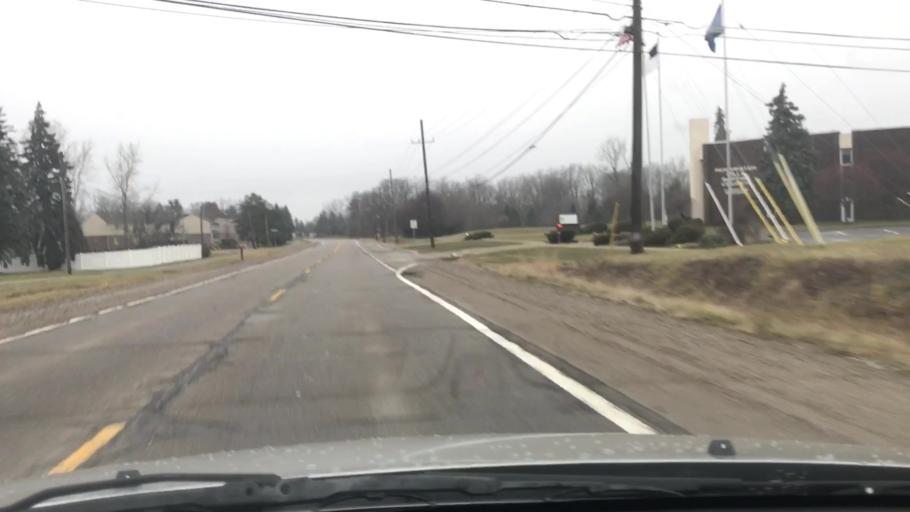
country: US
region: Michigan
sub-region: Oakland County
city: Troy
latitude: 42.6320
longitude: -83.1520
